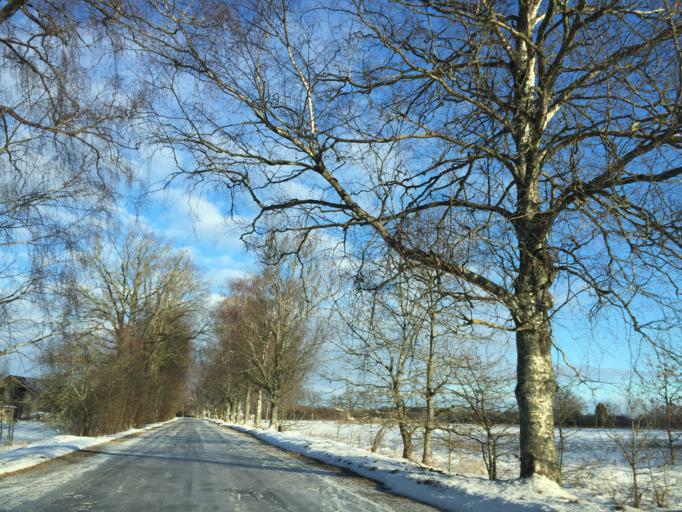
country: LV
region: Kegums
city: Kegums
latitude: 56.7415
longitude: 24.6663
